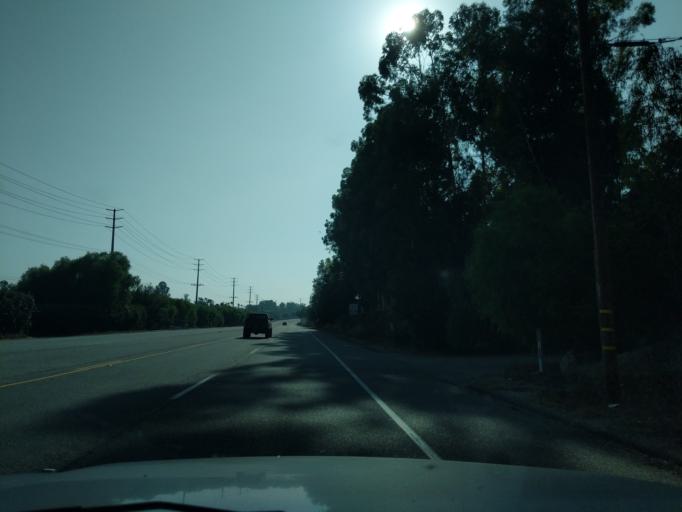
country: US
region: California
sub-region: Ventura County
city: Simi Valley
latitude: 34.2700
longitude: -118.8312
